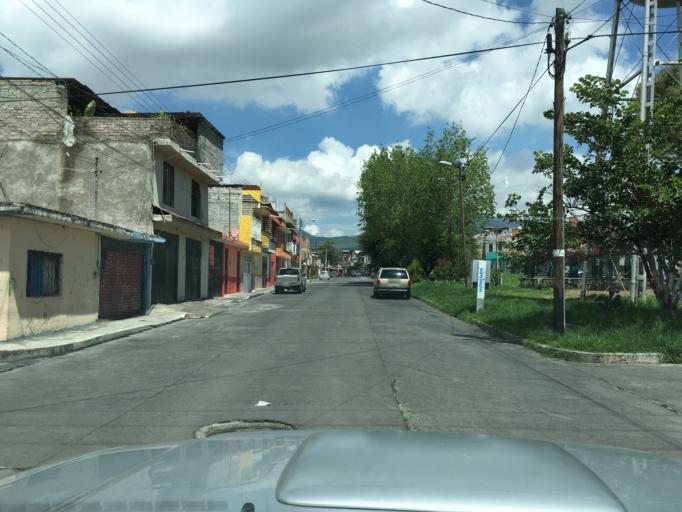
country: MX
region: Michoacan
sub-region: Tarimbaro
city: Real Hacienda (Metropolis)
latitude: 19.7285
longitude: -101.2006
